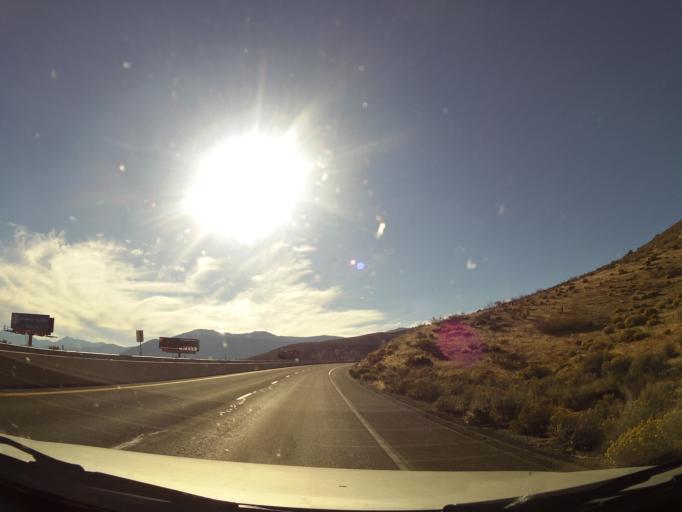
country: US
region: Nevada
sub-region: Douglas County
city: Indian Hills
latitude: 39.1151
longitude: -119.7831
